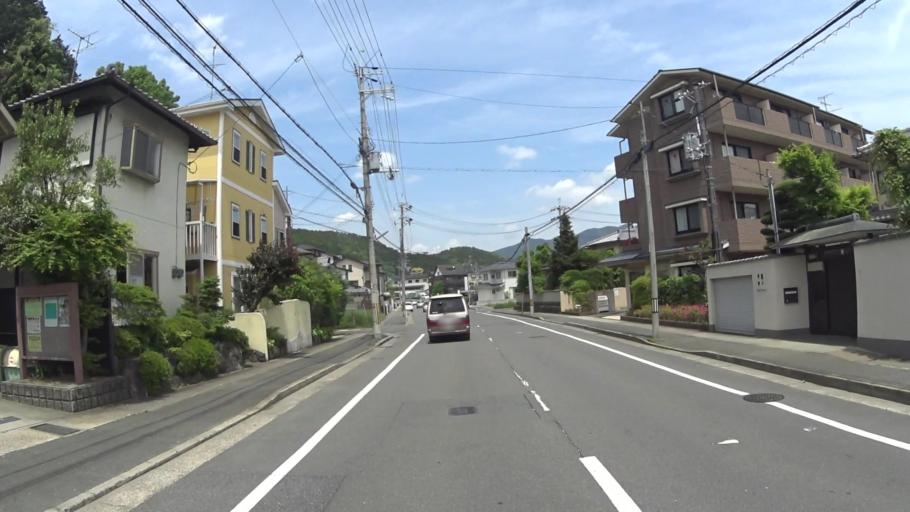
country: JP
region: Kyoto
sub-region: Kyoto-shi
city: Kamigyo-ku
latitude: 35.0671
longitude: 135.7763
